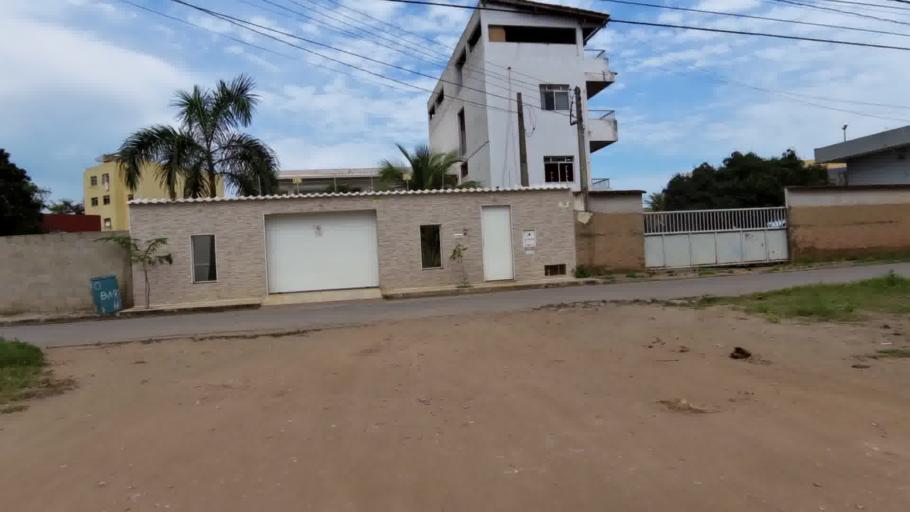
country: BR
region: Espirito Santo
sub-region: Piuma
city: Piuma
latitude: -20.8422
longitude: -40.7311
